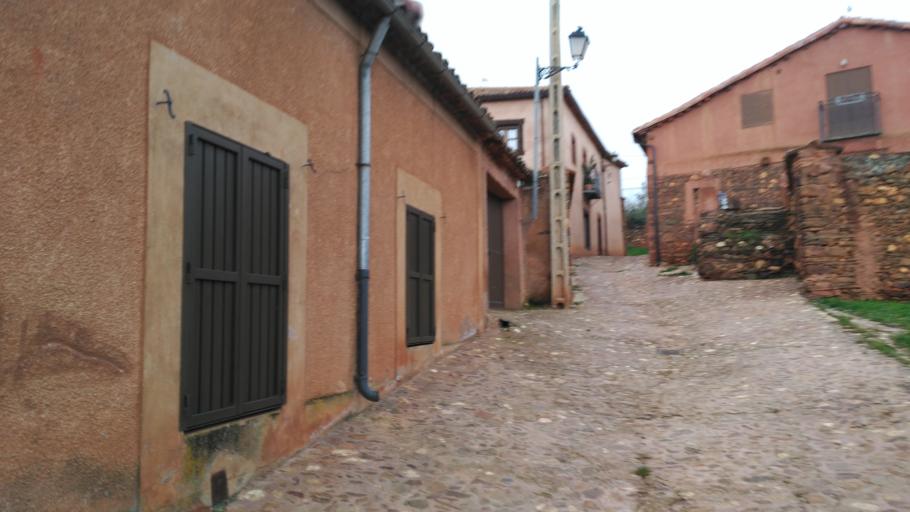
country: ES
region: Castille and Leon
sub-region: Provincia de Soria
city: Liceras
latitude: 41.3154
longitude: -3.3310
